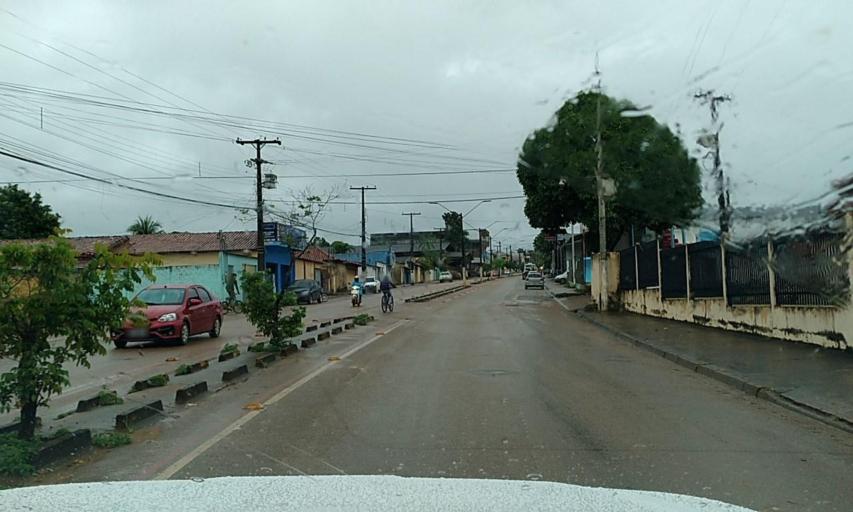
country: BR
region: Para
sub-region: Altamira
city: Altamira
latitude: -3.2120
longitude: -52.2270
